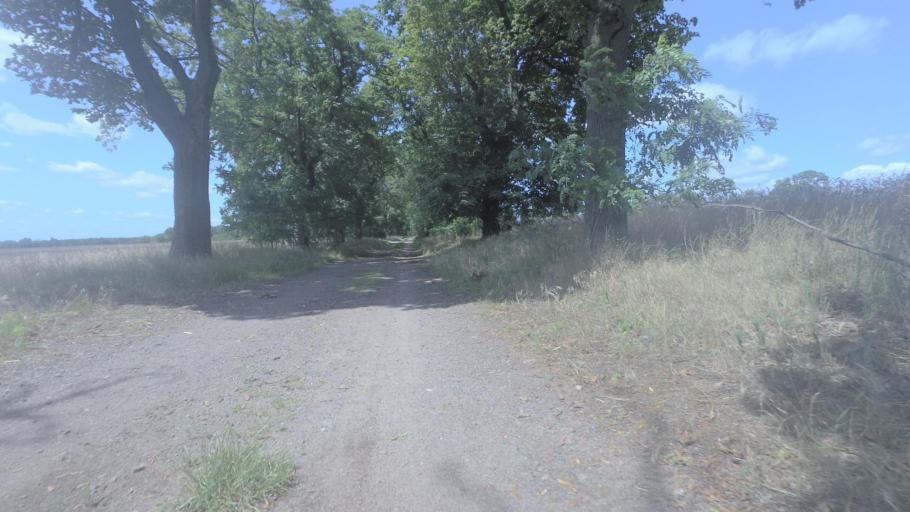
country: DE
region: Brandenburg
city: Am Mellensee
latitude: 52.2455
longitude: 13.3538
